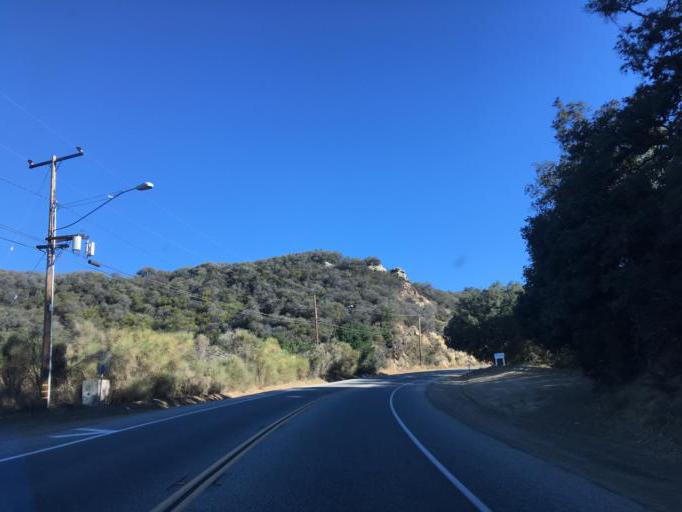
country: US
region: California
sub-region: Los Angeles County
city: Westlake Village
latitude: 34.0799
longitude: -118.8193
